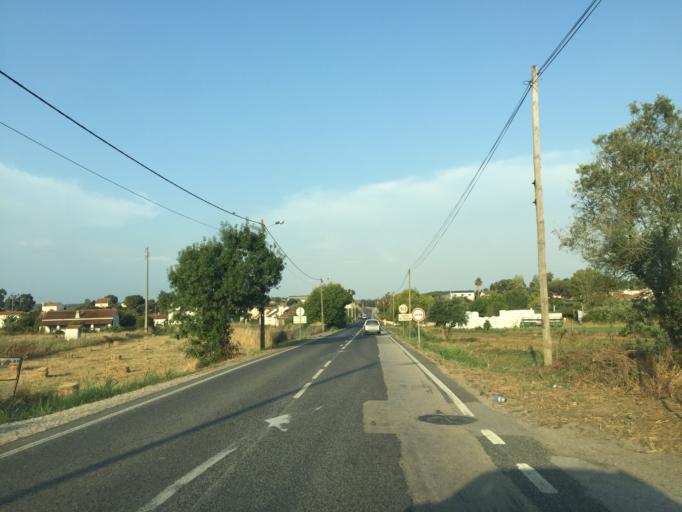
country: PT
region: Santarem
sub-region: Tomar
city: Tomar
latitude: 39.5506
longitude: -8.3839
